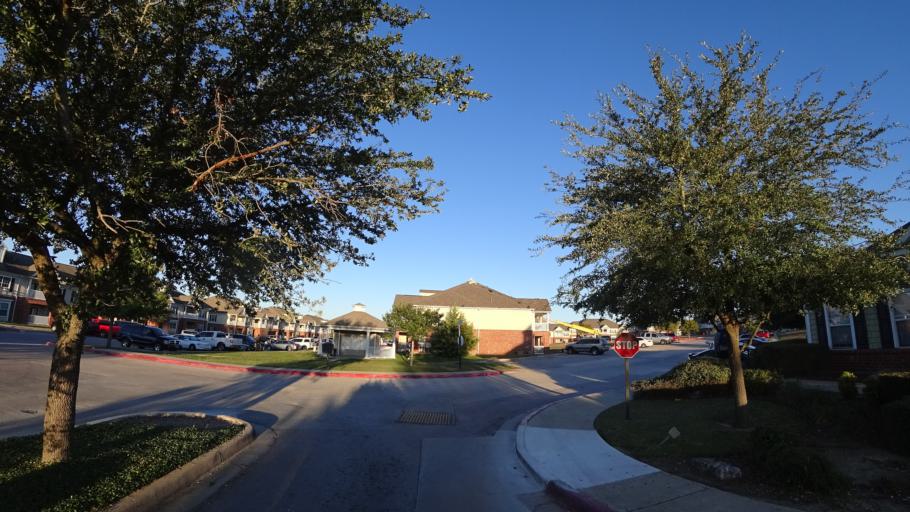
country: US
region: Texas
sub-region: Travis County
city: Hornsby Bend
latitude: 30.3068
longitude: -97.6219
